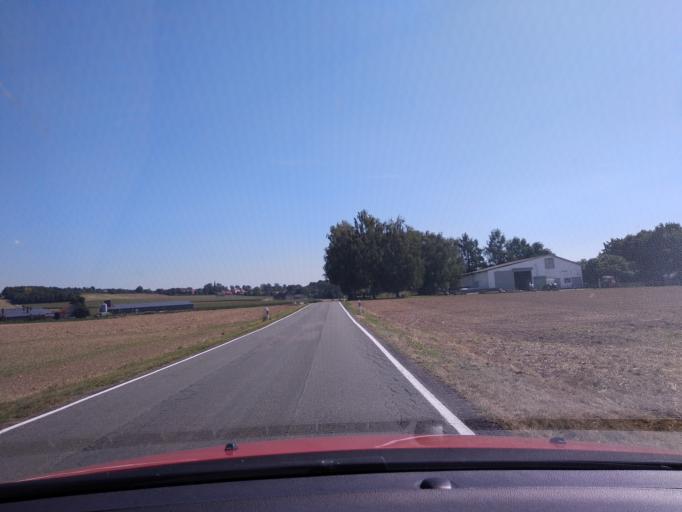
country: DE
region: North Rhine-Westphalia
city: Brakel
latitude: 51.6466
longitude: 9.1742
